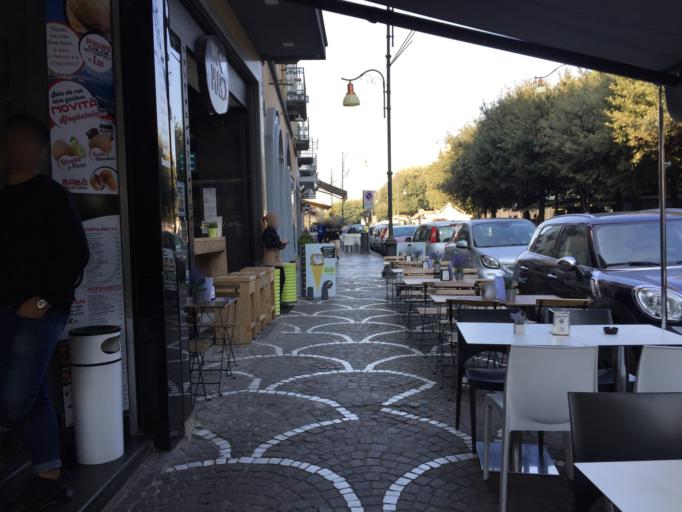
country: IT
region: Campania
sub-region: Provincia di Napoli
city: Pompei
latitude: 40.7492
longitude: 14.4966
